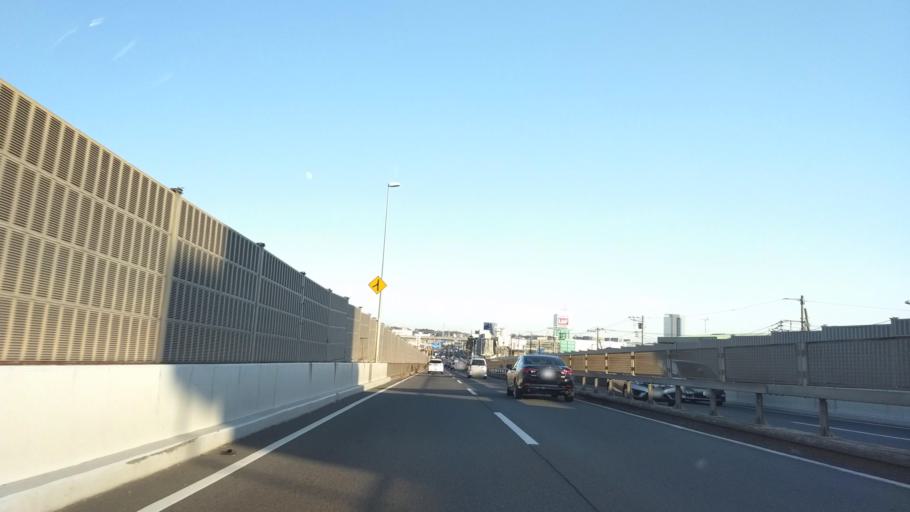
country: JP
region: Kanagawa
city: Atsugi
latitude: 35.4652
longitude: 139.3691
